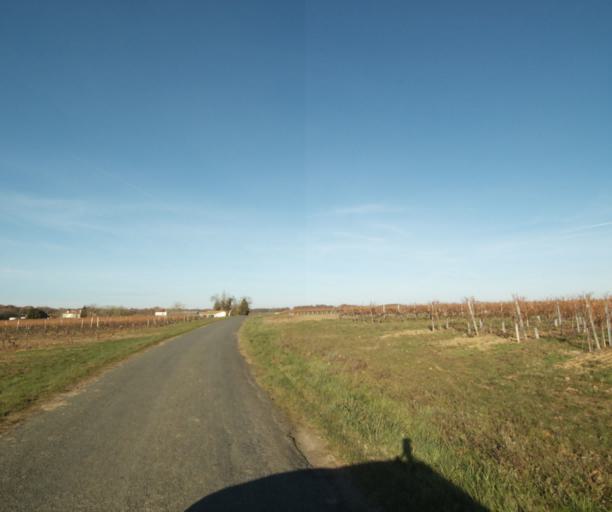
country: FR
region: Poitou-Charentes
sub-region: Departement de la Charente-Maritime
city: Cherac
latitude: 45.7225
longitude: -0.4390
